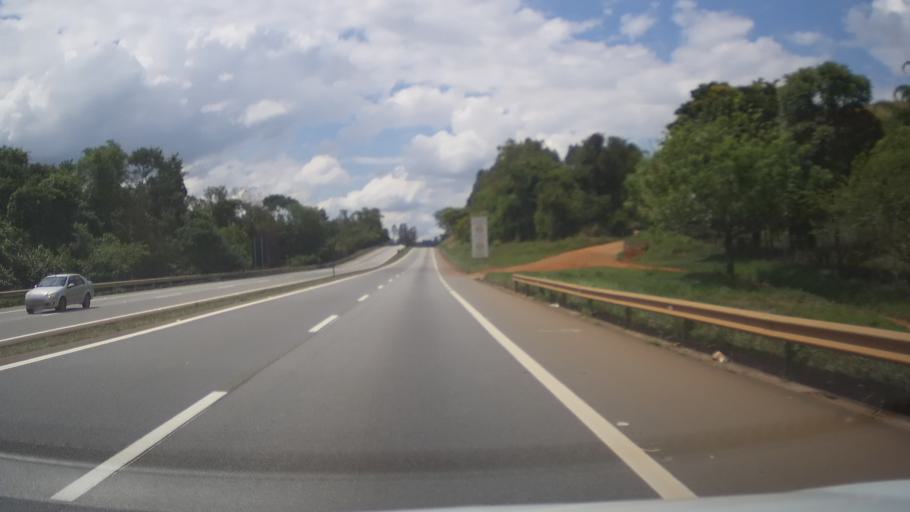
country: BR
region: Minas Gerais
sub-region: Nepomuceno
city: Nepomuceno
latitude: -21.2973
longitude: -45.1501
